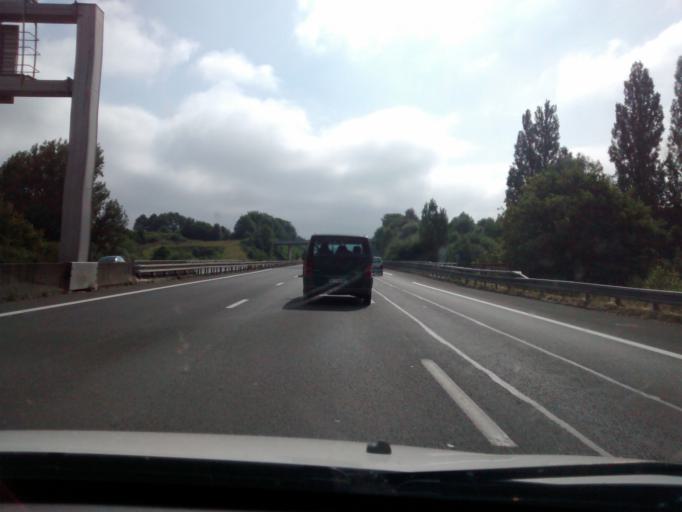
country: FR
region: Pays de la Loire
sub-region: Departement de la Sarthe
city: Neuville-sur-Sarthe
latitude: 48.0581
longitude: 0.2048
